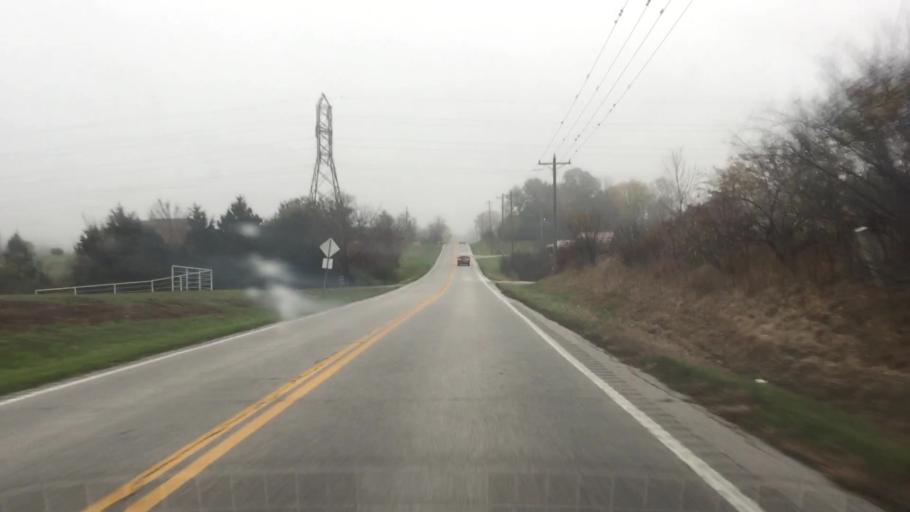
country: US
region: Missouri
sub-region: Callaway County
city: Fulton
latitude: 38.8581
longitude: -91.9942
